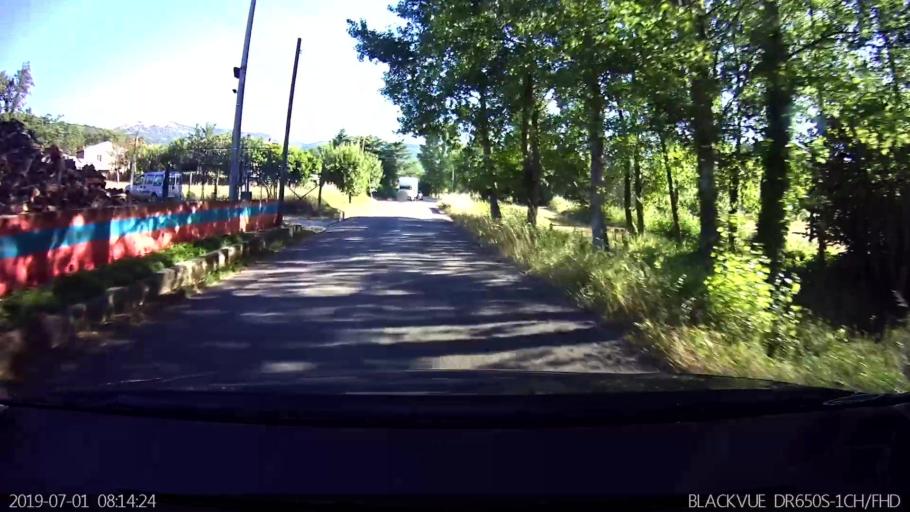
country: IT
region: Latium
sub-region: Provincia di Frosinone
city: Veroli
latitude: 41.6958
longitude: 13.4281
